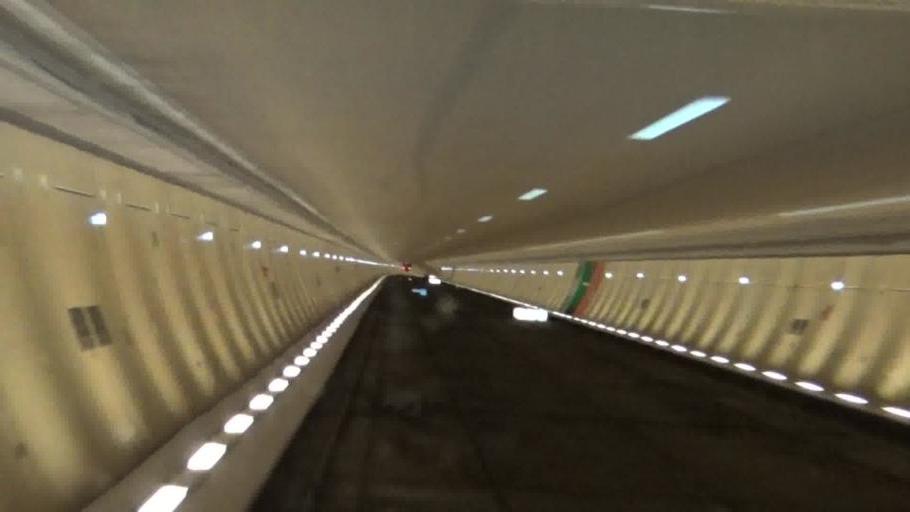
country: FR
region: Ile-de-France
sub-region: Departement des Yvelines
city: Viroflay
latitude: 48.8117
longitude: 2.1603
